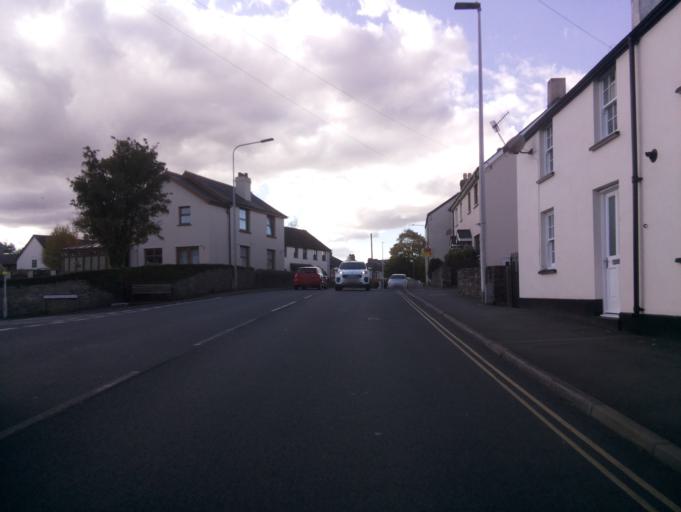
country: GB
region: Wales
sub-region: Sir Powys
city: Brecon
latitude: 51.9449
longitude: -3.4042
